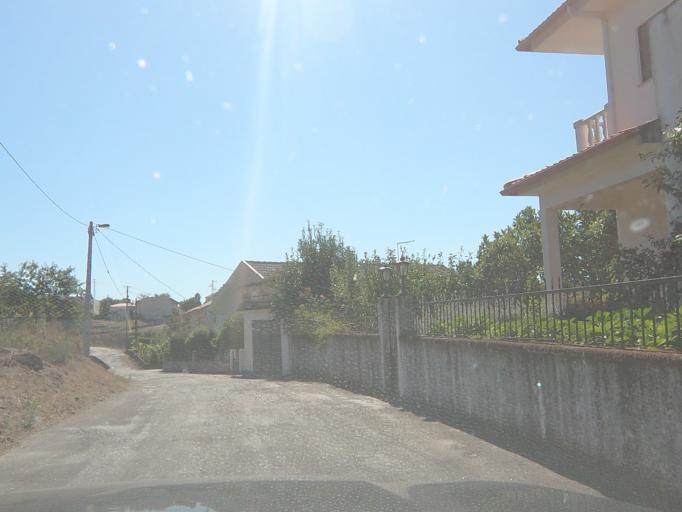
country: PT
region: Vila Real
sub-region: Vila Real
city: Vila Real
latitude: 41.3190
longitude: -7.7369
